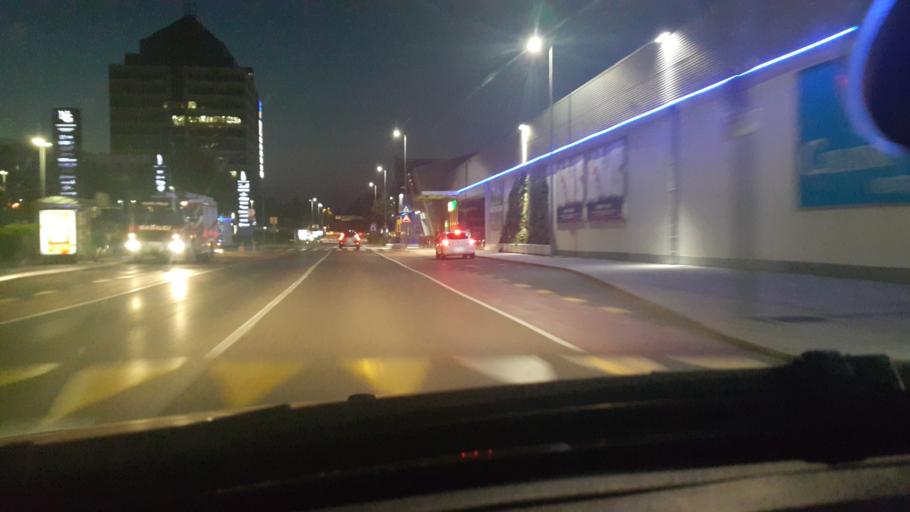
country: SI
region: Ljubljana
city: Ljubljana
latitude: 46.0666
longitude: 14.5422
